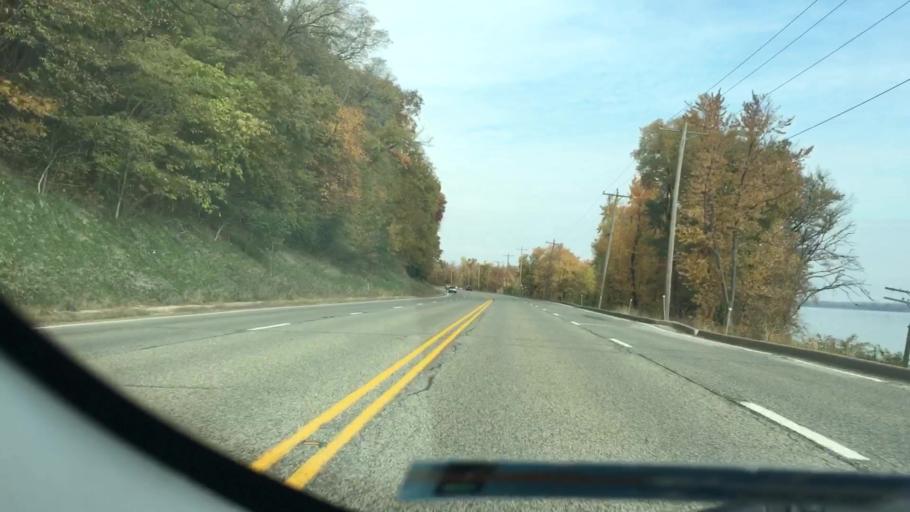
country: US
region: Illinois
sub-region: Peoria County
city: Peoria Heights
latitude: 40.7328
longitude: -89.5514
